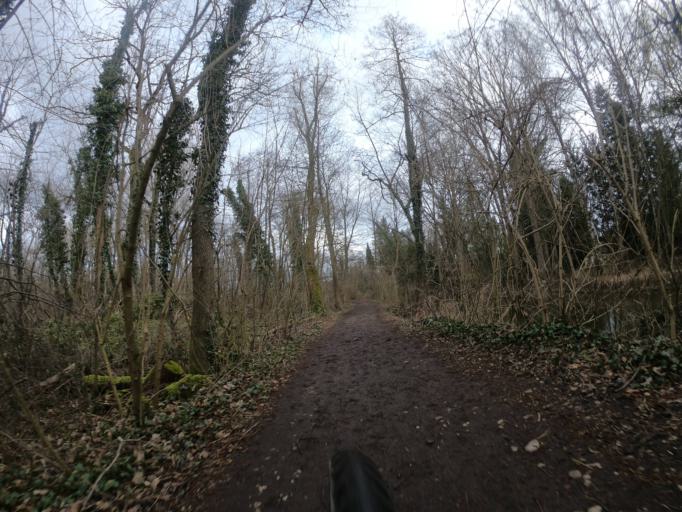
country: DE
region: Bavaria
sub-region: Upper Bavaria
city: Emmering
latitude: 48.1810
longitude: 11.2746
